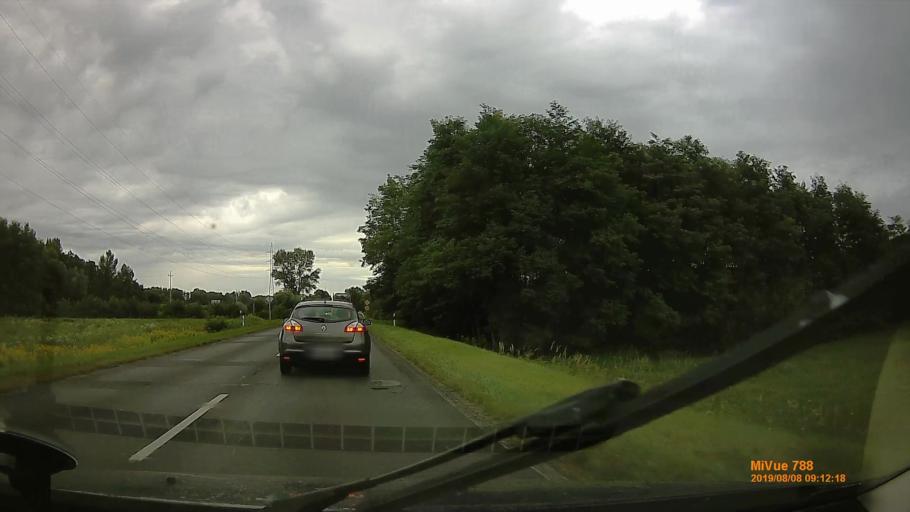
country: HU
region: Zala
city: Zalaegerszeg
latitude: 46.7946
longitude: 16.8562
